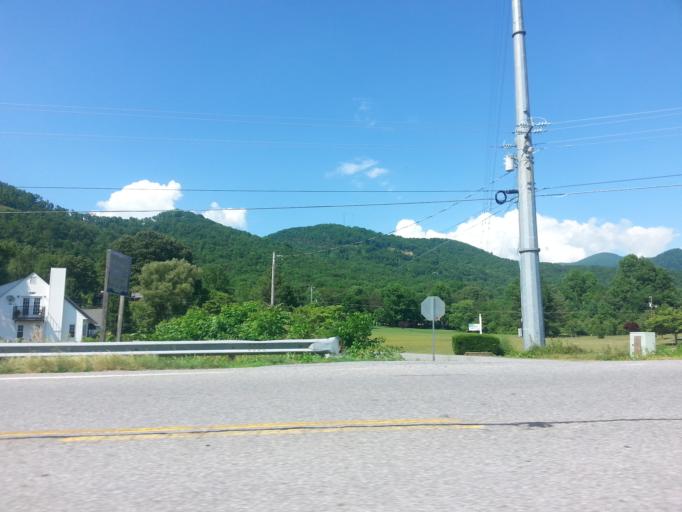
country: US
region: Georgia
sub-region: Towns County
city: Hiawassee
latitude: 34.9398
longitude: -83.7419
